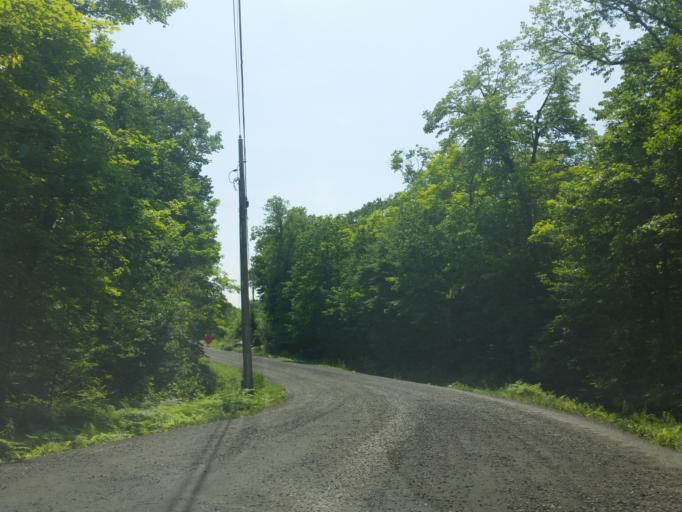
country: CA
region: Ontario
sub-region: Parry Sound District
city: Parry Sound
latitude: 45.4416
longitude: -80.0071
